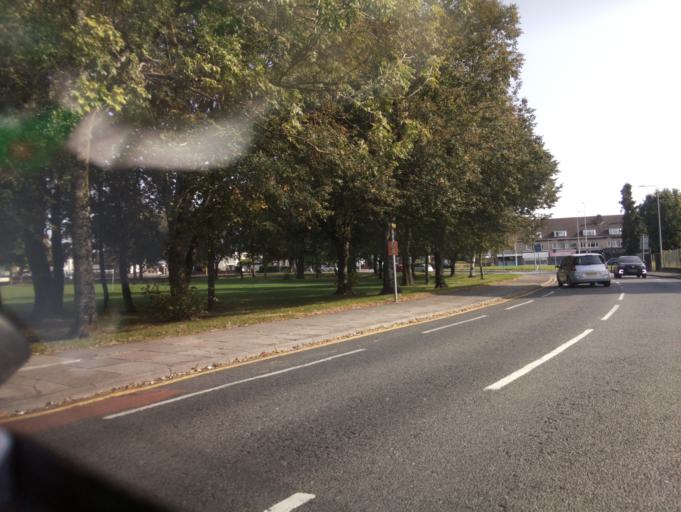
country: GB
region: Wales
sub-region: Cardiff
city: Cardiff
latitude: 51.5106
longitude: -3.1312
